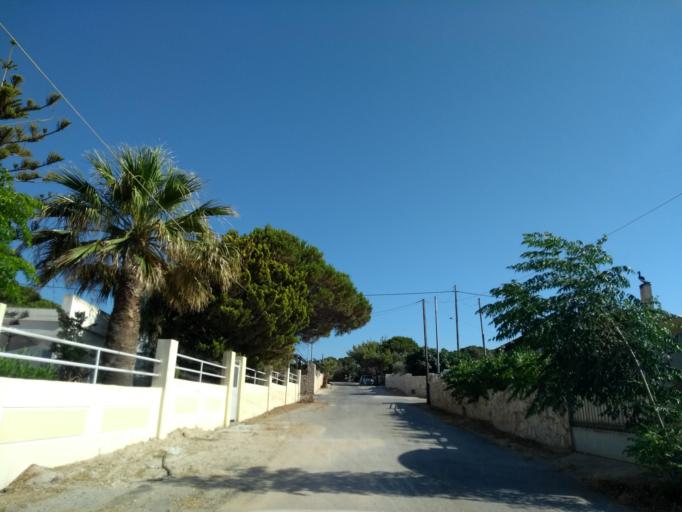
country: GR
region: Crete
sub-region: Nomos Chanias
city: Pithari
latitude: 35.5907
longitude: 24.0925
